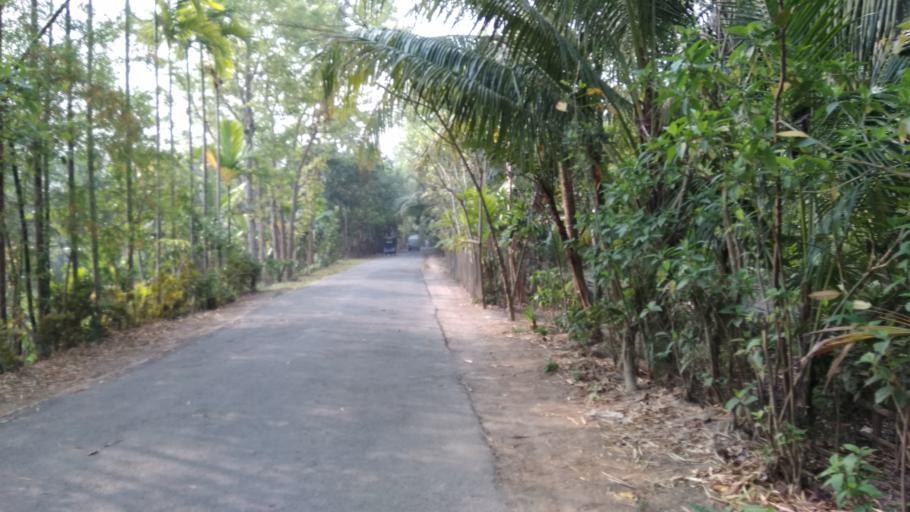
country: BD
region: Barisal
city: Mehendiganj
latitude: 22.9523
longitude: 90.4156
